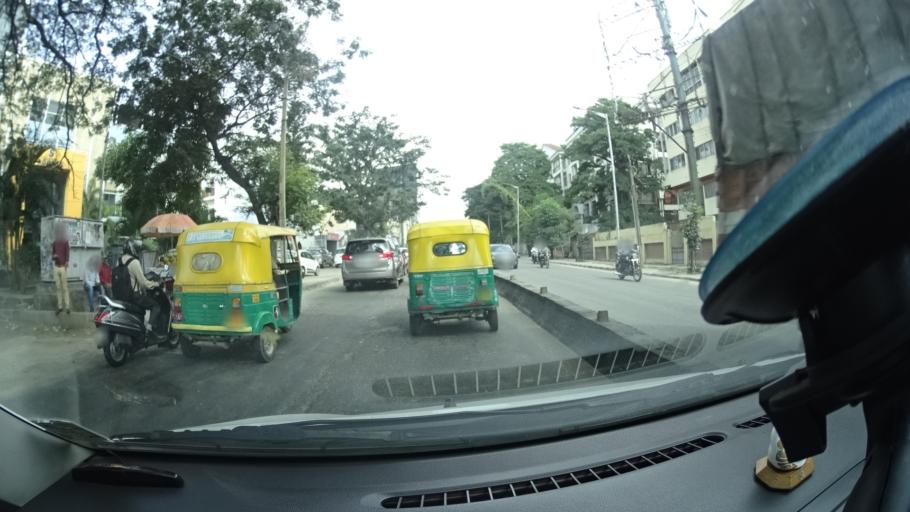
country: IN
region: Karnataka
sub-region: Bangalore Urban
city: Bangalore
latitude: 12.9834
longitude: 77.6388
